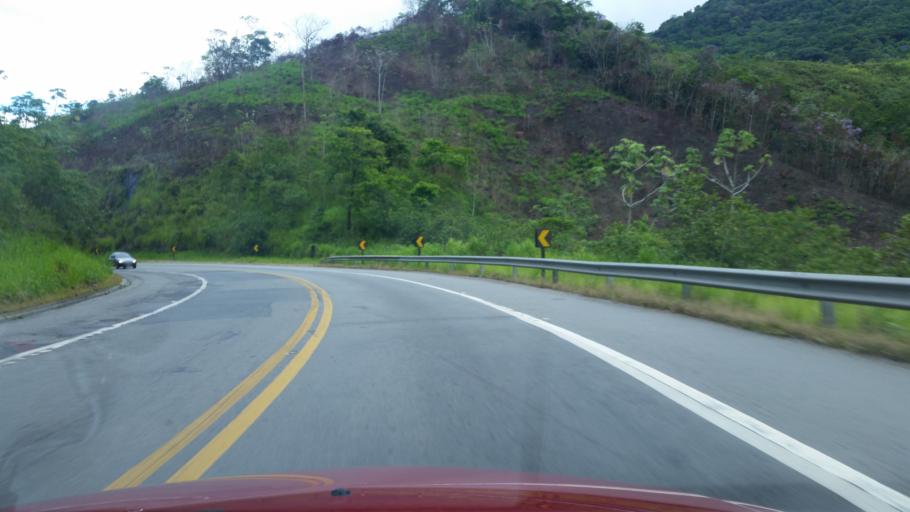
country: BR
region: Sao Paulo
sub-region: Miracatu
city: Miracatu
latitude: -24.2652
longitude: -47.3065
